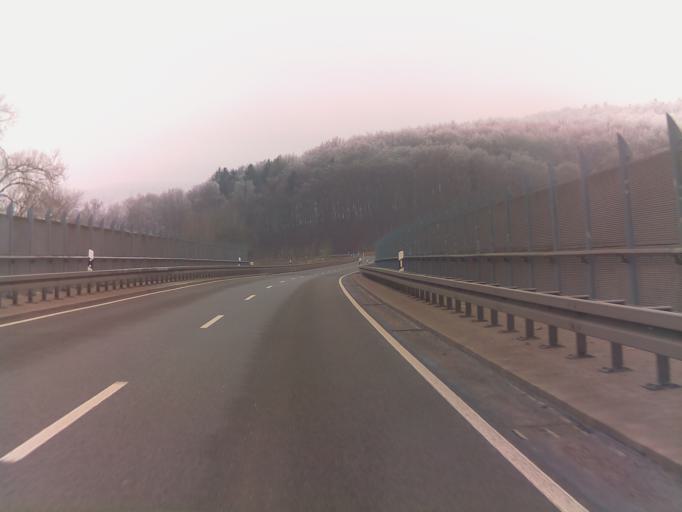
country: DE
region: Thuringia
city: Untermassfeld
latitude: 50.5421
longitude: 10.4056
